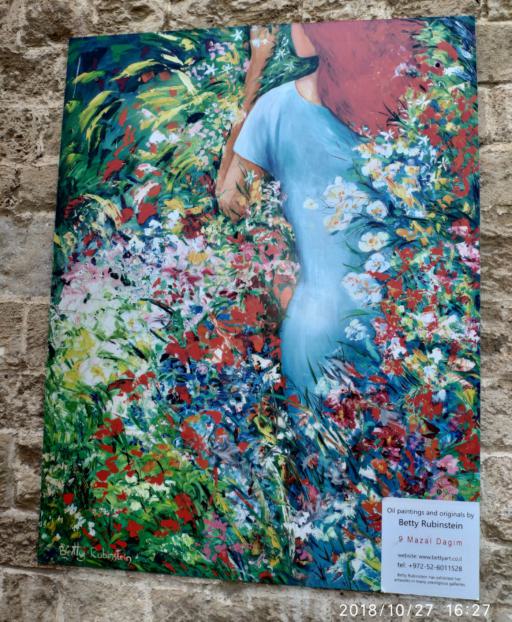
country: IL
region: Tel Aviv
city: Yafo
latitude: 32.0535
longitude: 34.7521
